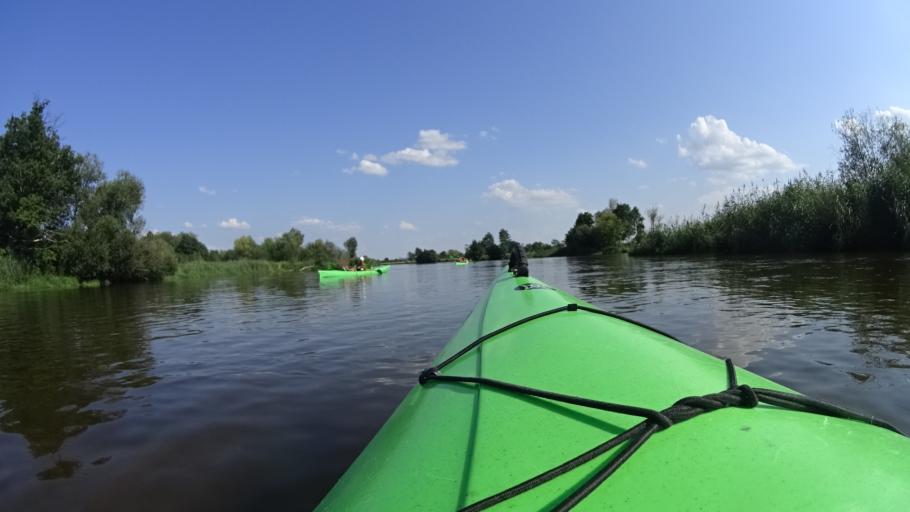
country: PL
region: Masovian Voivodeship
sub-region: Powiat bialobrzeski
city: Bialobrzegi
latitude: 51.6631
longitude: 20.9259
